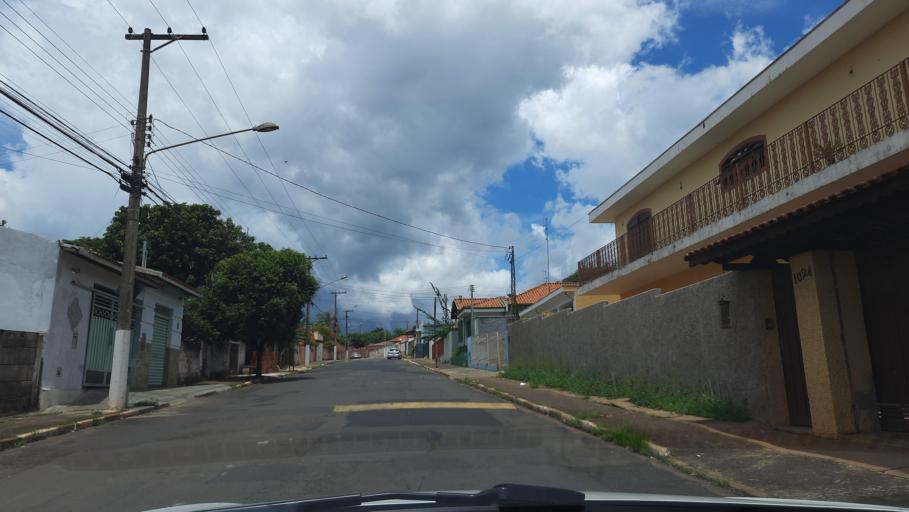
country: BR
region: Sao Paulo
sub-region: Casa Branca
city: Casa Branca
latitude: -21.7806
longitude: -47.0940
